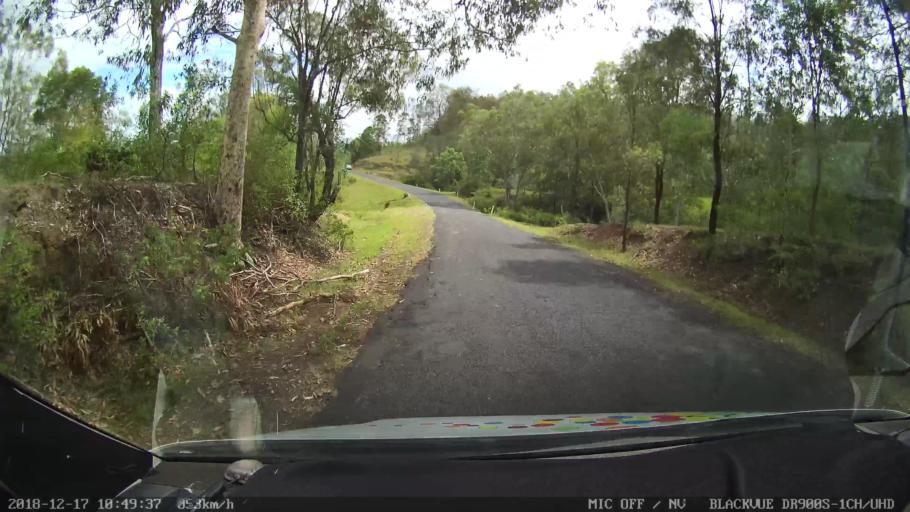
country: AU
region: New South Wales
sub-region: Clarence Valley
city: Gordon
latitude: -28.8645
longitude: 152.5740
